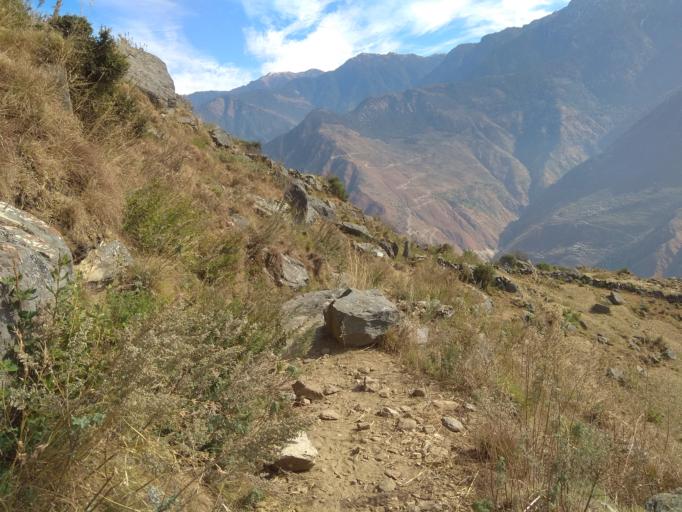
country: NP
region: Mid Western
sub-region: Bheri Zone
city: Dailekh
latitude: 29.2959
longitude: 81.7211
